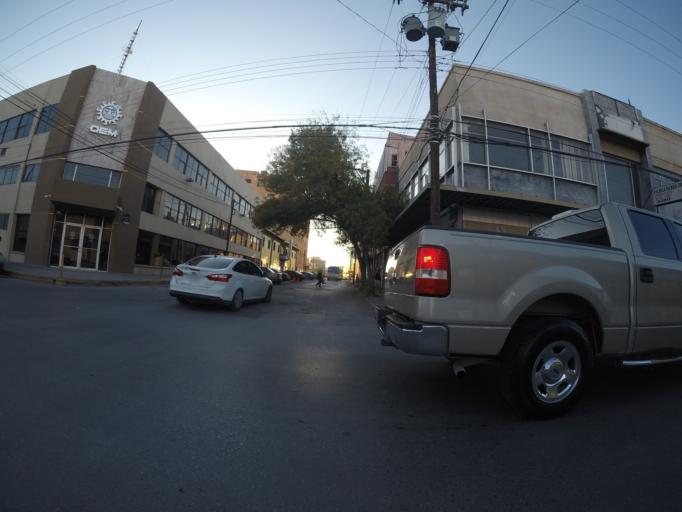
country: MX
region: Chihuahua
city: Ciudad Juarez
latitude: 31.7373
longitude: -106.4804
